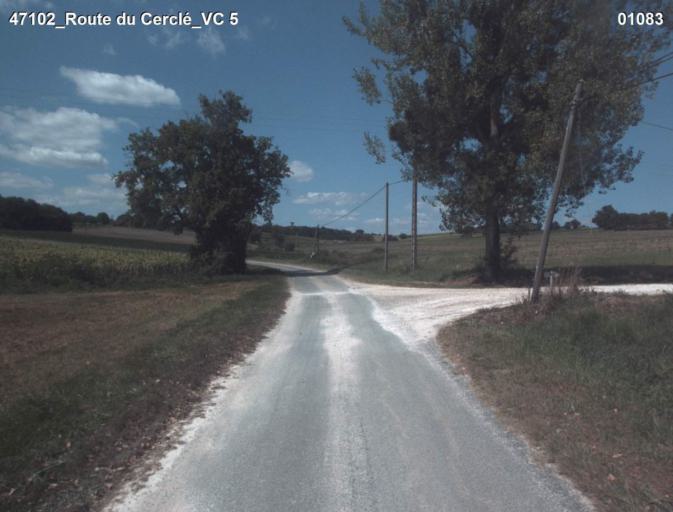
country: FR
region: Aquitaine
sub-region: Departement du Lot-et-Garonne
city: Laplume
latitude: 44.0758
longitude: 0.4500
